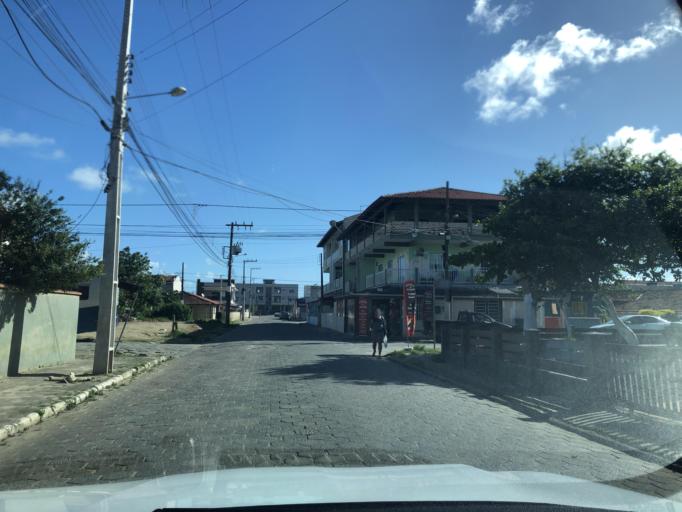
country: BR
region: Santa Catarina
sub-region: Sao Francisco Do Sul
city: Sao Francisco do Sul
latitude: -26.2306
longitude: -48.5108
